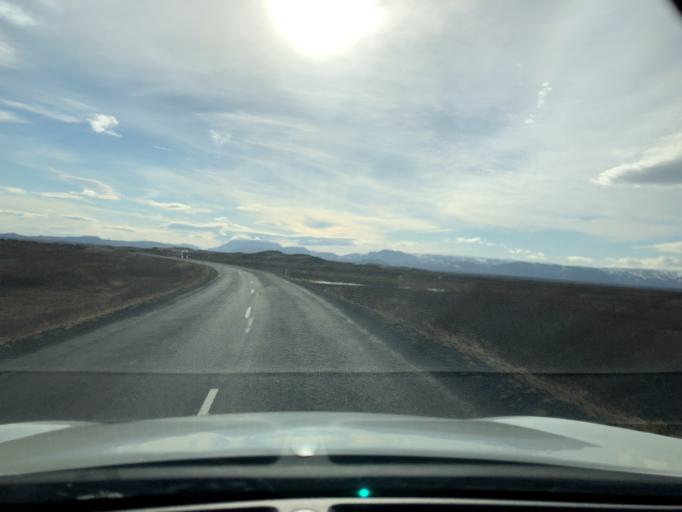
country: IS
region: Northeast
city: Laugar
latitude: 65.5707
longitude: -17.0794
